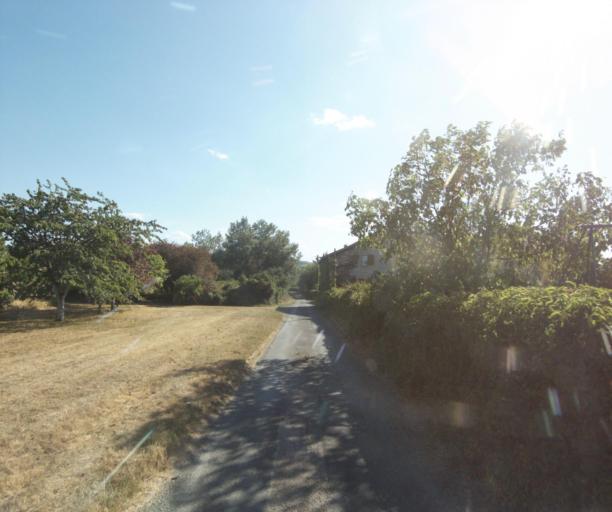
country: FR
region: Rhone-Alpes
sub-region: Departement du Rhone
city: Lentilly
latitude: 45.8191
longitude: 4.6771
